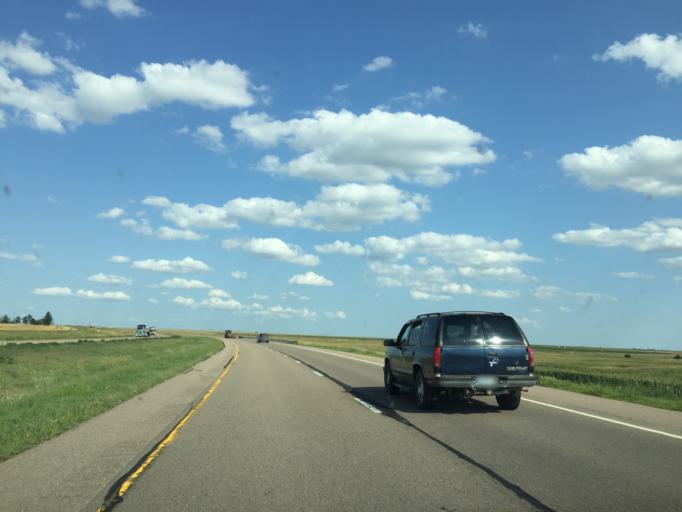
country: US
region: Kansas
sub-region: Trego County
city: WaKeeney
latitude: 39.0247
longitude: -100.1704
